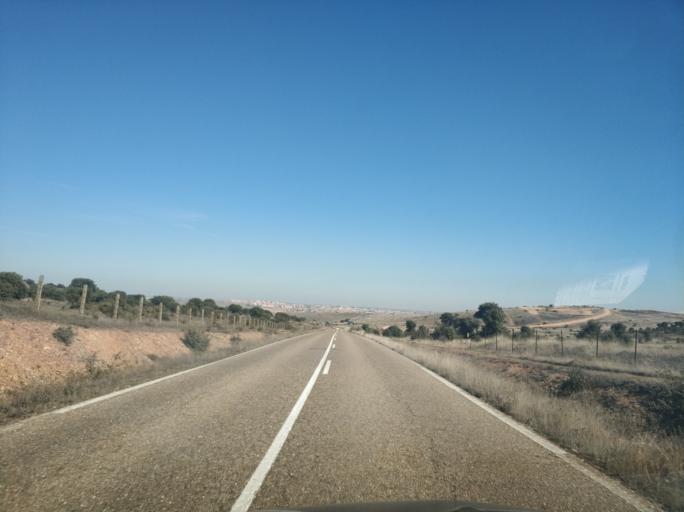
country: ES
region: Castille and Leon
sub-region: Provincia de Salamanca
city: Doninos de Salamanca
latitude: 40.9330
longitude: -5.7249
